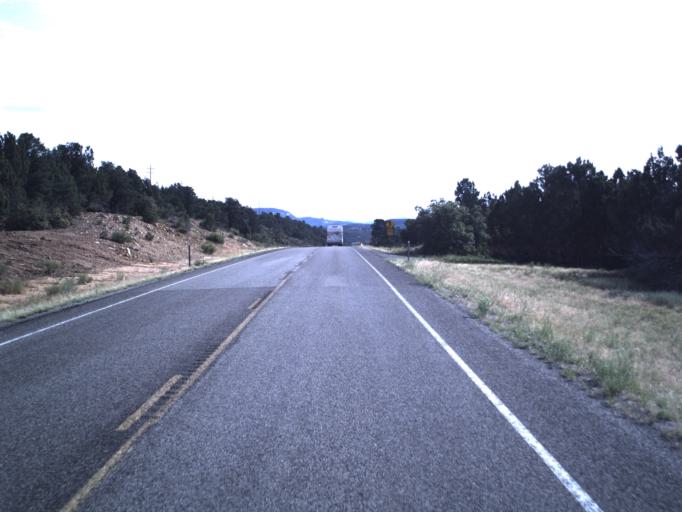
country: US
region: Utah
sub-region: Washington County
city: Hildale
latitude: 37.2499
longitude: -112.8001
